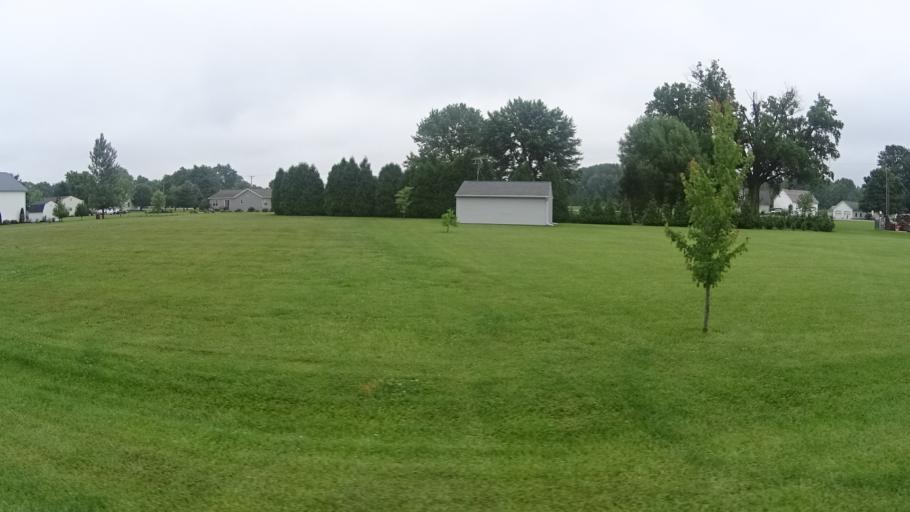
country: US
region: Ohio
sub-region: Erie County
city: Milan
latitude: 41.3163
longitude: -82.6029
